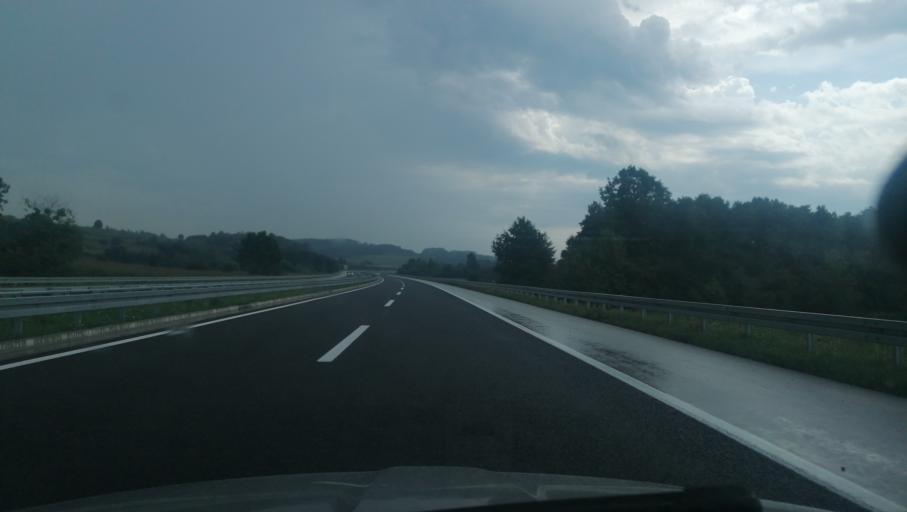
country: BA
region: Republika Srpska
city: Maglajani
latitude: 44.8702
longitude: 17.4206
